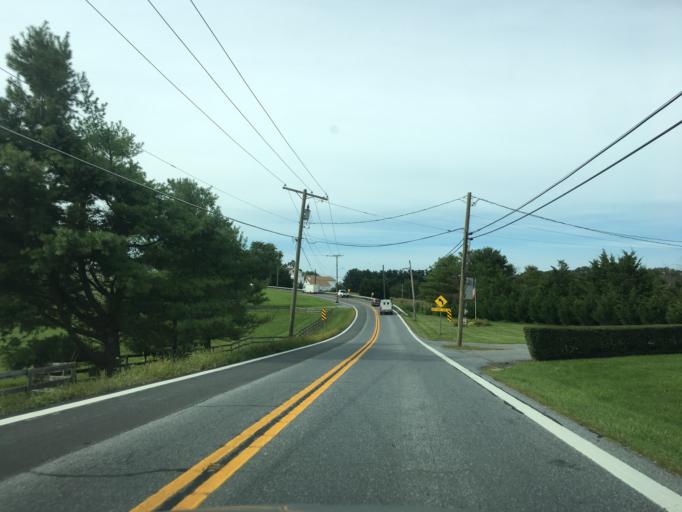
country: US
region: Maryland
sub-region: Carroll County
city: Hampstead
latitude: 39.5919
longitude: -76.7337
